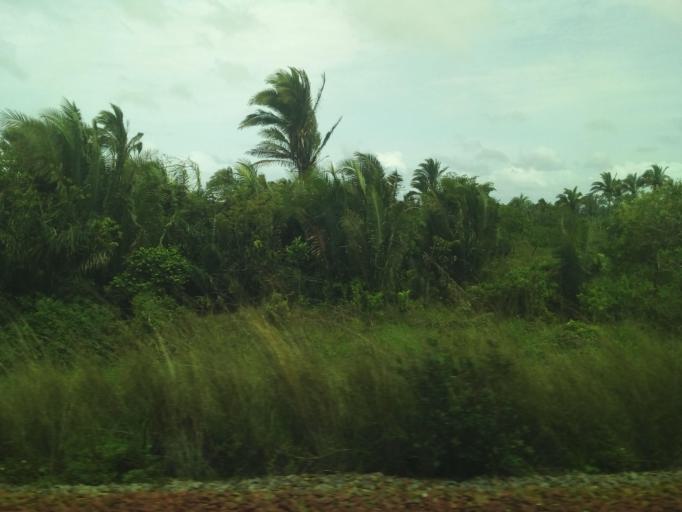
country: BR
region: Maranhao
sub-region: Arari
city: Arari
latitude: -3.5266
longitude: -44.6380
